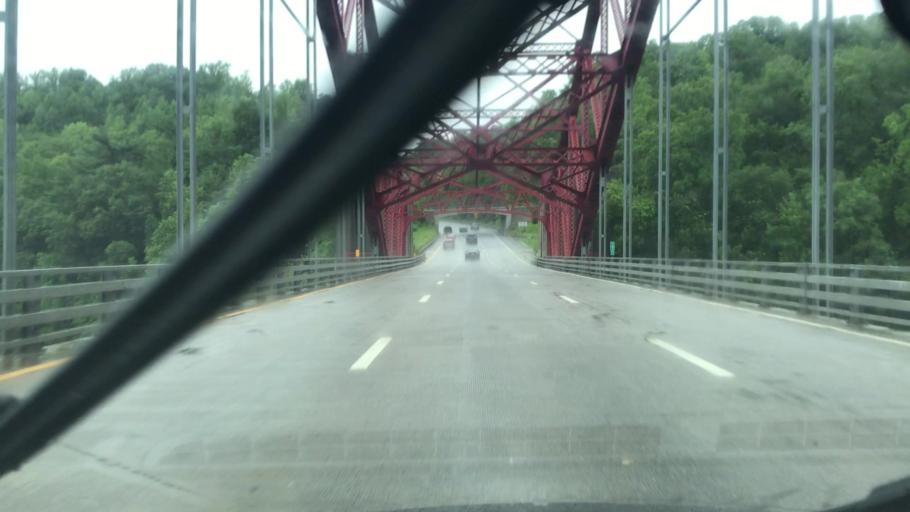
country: US
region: New York
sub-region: Westchester County
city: Yorktown Heights
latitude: 41.2381
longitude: -73.8129
